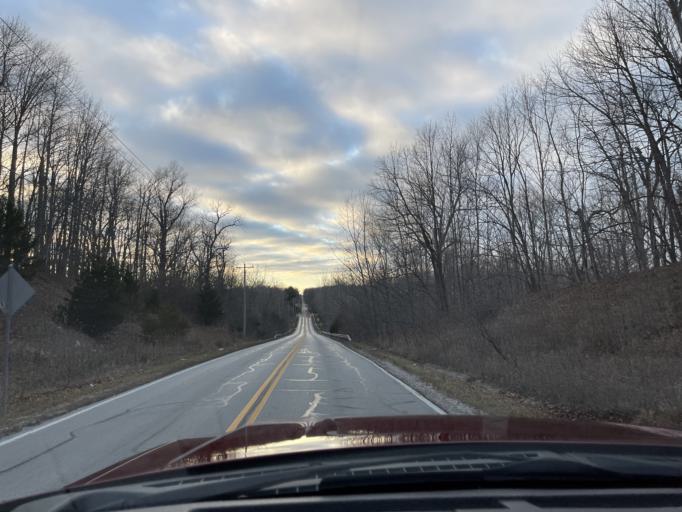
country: US
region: Indiana
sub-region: Hendricks County
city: Avon
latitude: 39.7771
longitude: -86.4165
